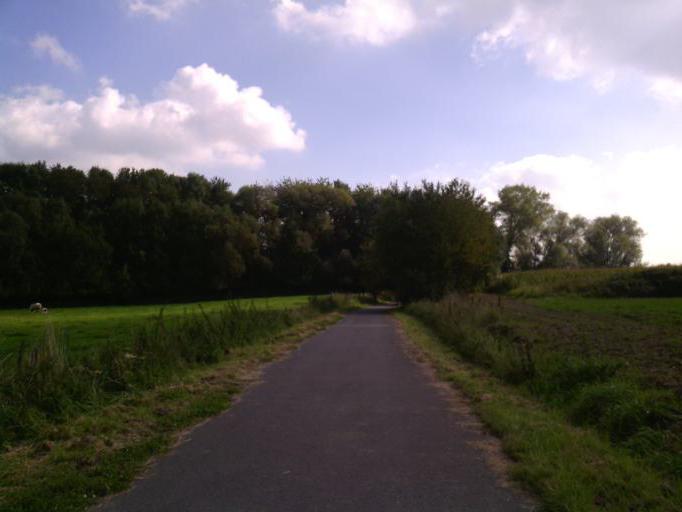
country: BE
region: Wallonia
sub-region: Province du Hainaut
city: Flobecq
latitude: 50.7430
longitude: 3.7391
